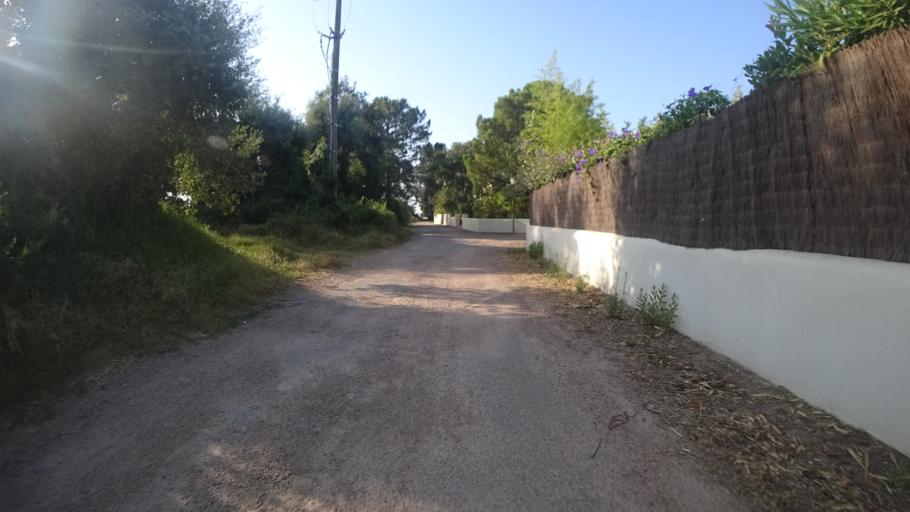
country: FR
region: Corsica
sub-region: Departement de la Corse-du-Sud
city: Porto-Vecchio
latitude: 41.6396
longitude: 9.3470
